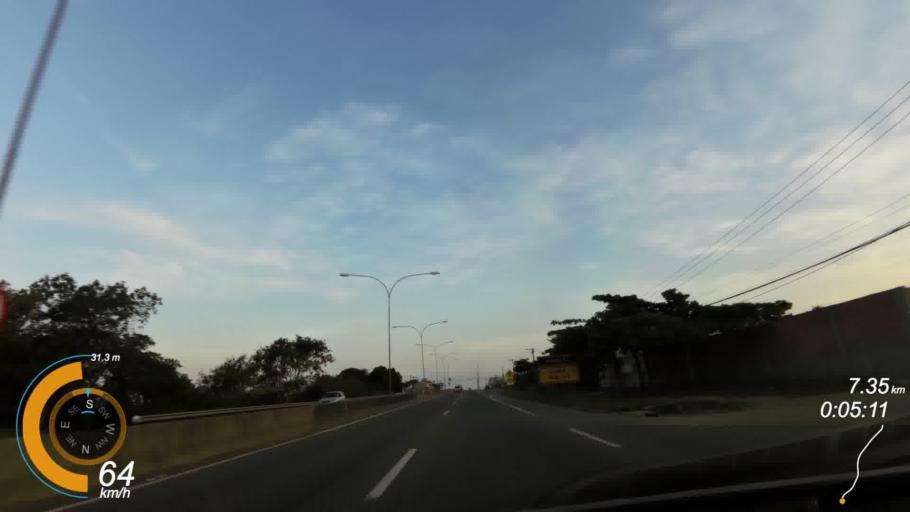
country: BR
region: Espirito Santo
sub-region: Viana
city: Viana
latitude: -20.5048
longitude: -40.3642
